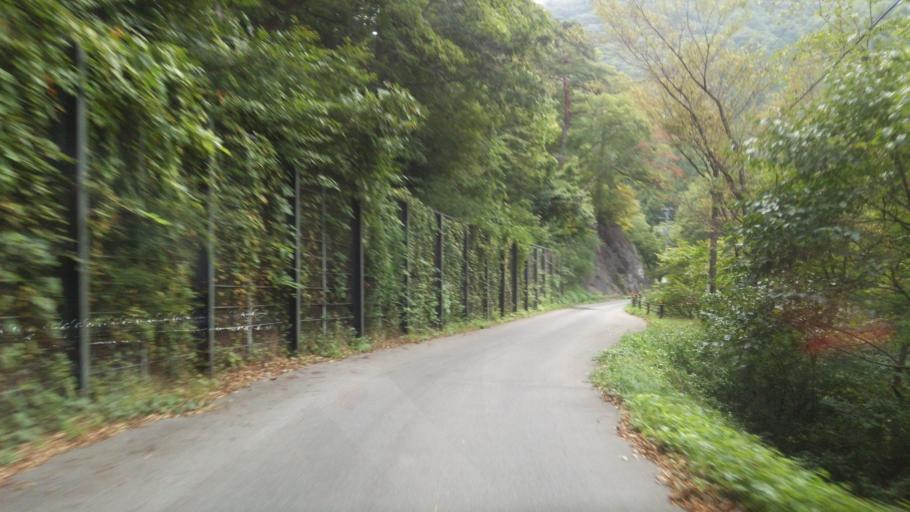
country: JP
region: Fukushima
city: Inawashiro
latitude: 37.3814
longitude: 139.9399
